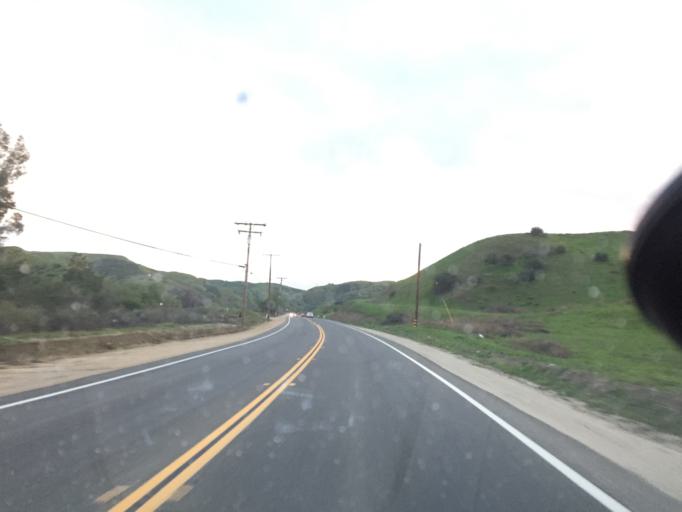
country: US
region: California
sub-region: San Bernardino County
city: Redlands
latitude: 33.9884
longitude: -117.1554
